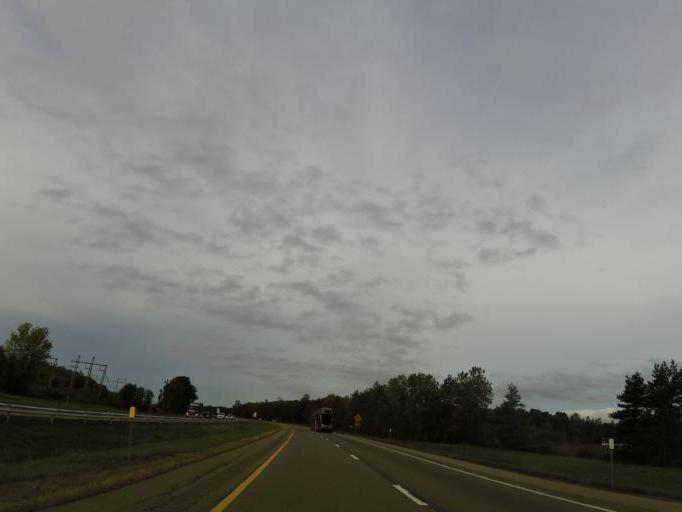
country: US
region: New York
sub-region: Chautauqua County
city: Silver Creek
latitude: 42.5123
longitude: -79.1969
